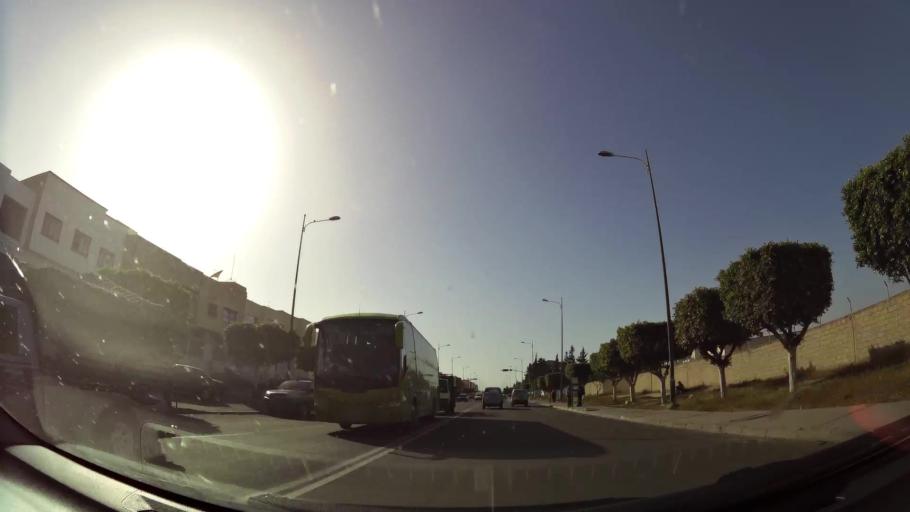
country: MA
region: Souss-Massa-Draa
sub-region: Inezgane-Ait Mellou
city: Inezgane
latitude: 30.3835
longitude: -9.5200
